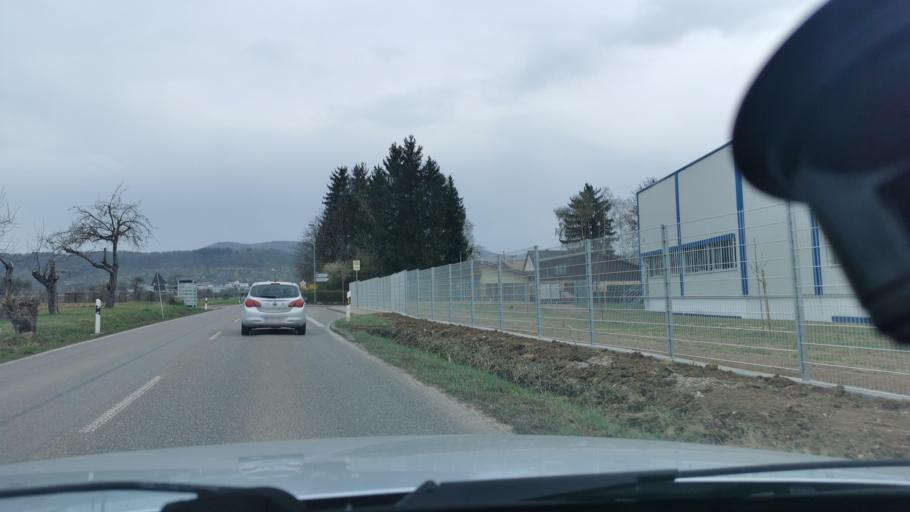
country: DE
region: Baden-Wuerttemberg
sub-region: Regierungsbezirk Stuttgart
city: Weilheim an der Teck
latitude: 48.6247
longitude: 9.5307
